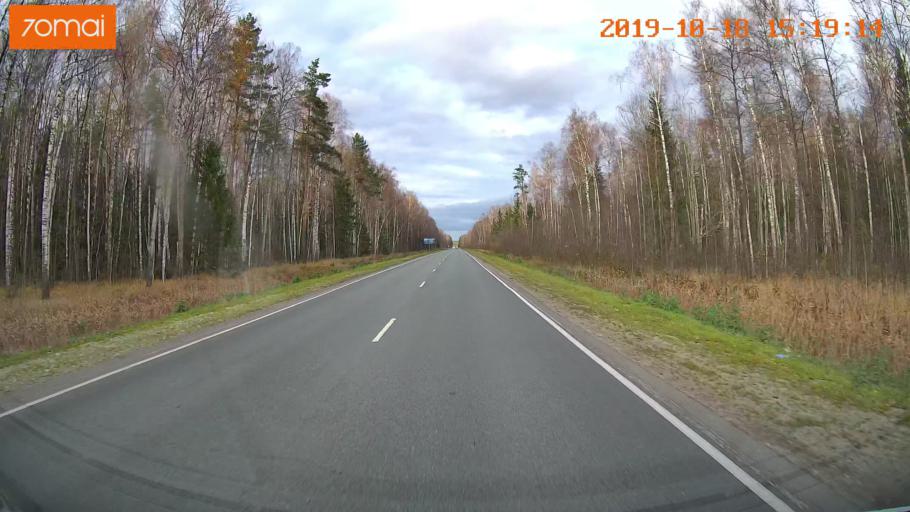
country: RU
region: Vladimir
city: Anopino
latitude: 55.6701
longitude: 40.7362
